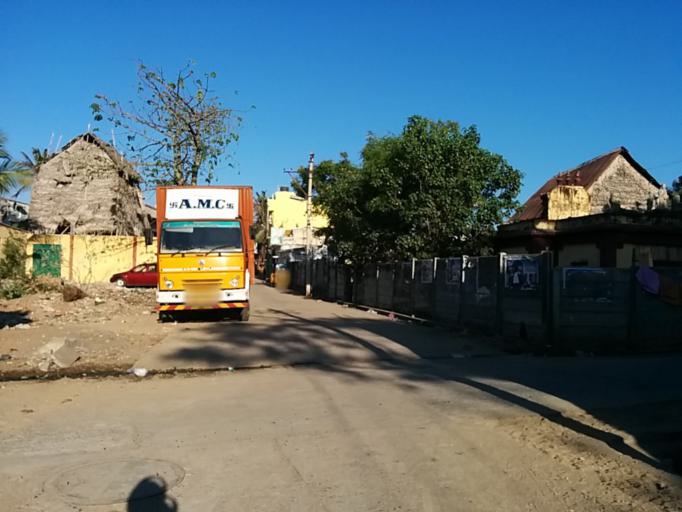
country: IN
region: Pondicherry
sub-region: Puducherry
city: Puducherry
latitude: 11.9183
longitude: 79.8311
